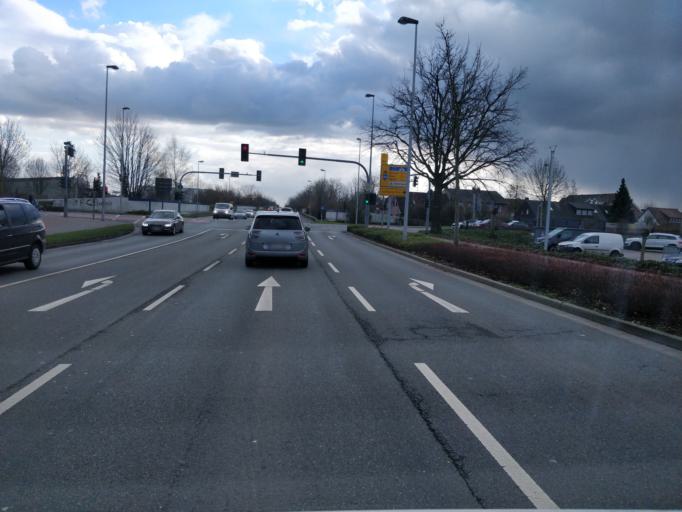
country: DE
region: North Rhine-Westphalia
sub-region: Regierungsbezirk Dusseldorf
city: Bocholt
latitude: 51.8376
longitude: 6.5972
